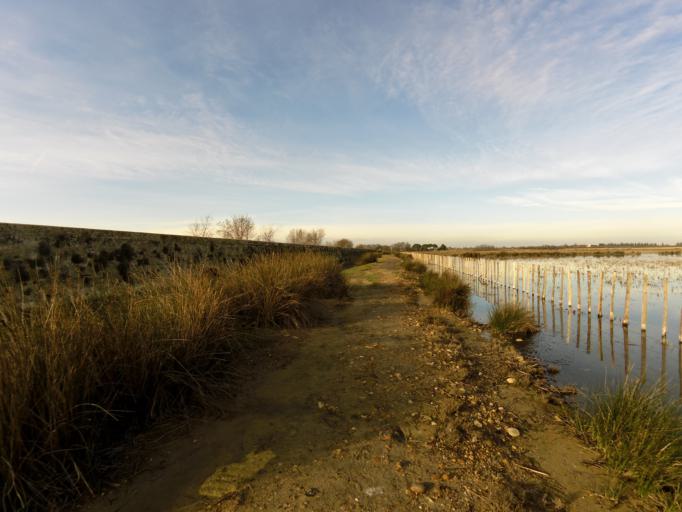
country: FR
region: Languedoc-Roussillon
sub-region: Departement du Gard
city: Aigues-Mortes
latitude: 43.5936
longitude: 4.2091
